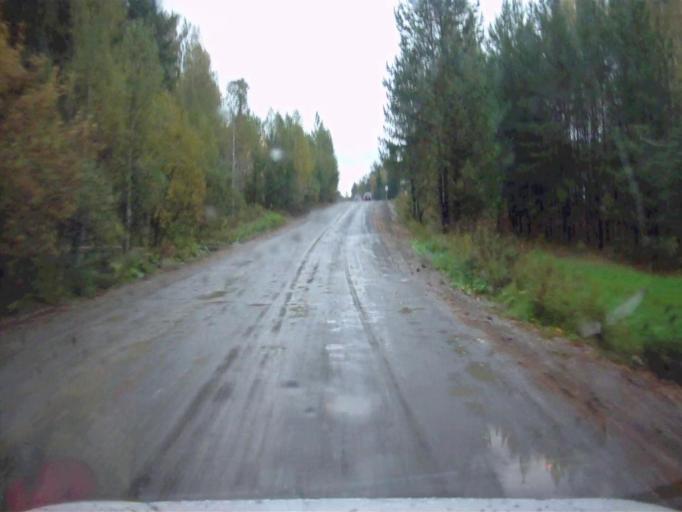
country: RU
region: Chelyabinsk
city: Kyshtym
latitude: 55.7526
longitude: 60.4868
